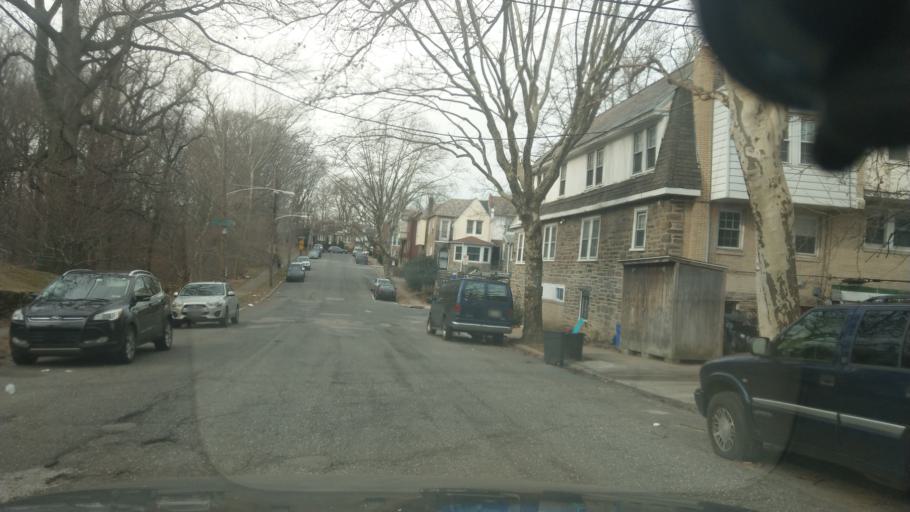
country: US
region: Pennsylvania
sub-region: Montgomery County
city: Jenkintown
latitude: 40.0445
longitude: -75.1318
